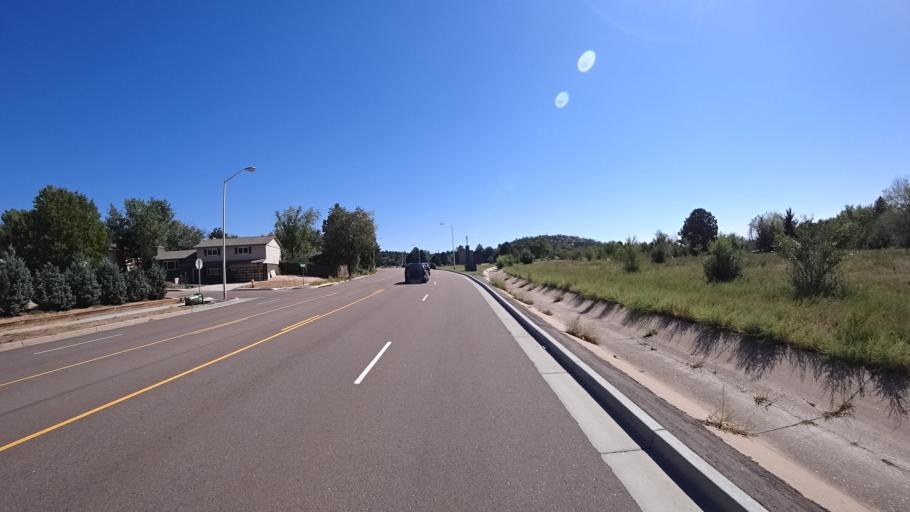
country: US
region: Colorado
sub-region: El Paso County
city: Cimarron Hills
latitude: 38.8611
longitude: -104.7523
